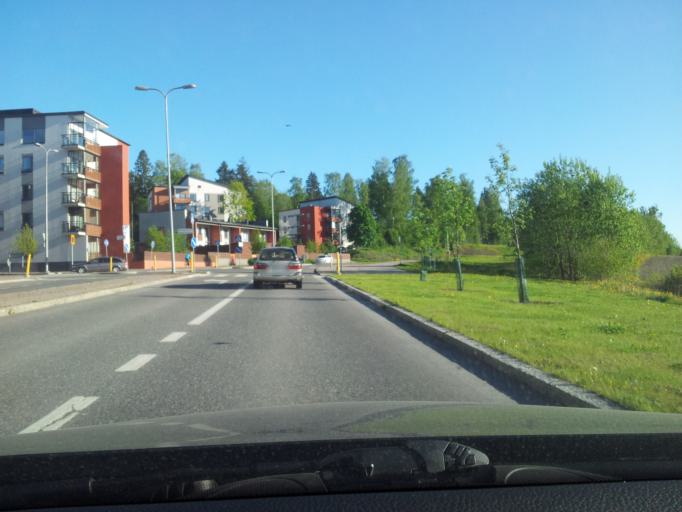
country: FI
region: Uusimaa
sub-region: Helsinki
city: Kilo
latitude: 60.2147
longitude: 24.8003
